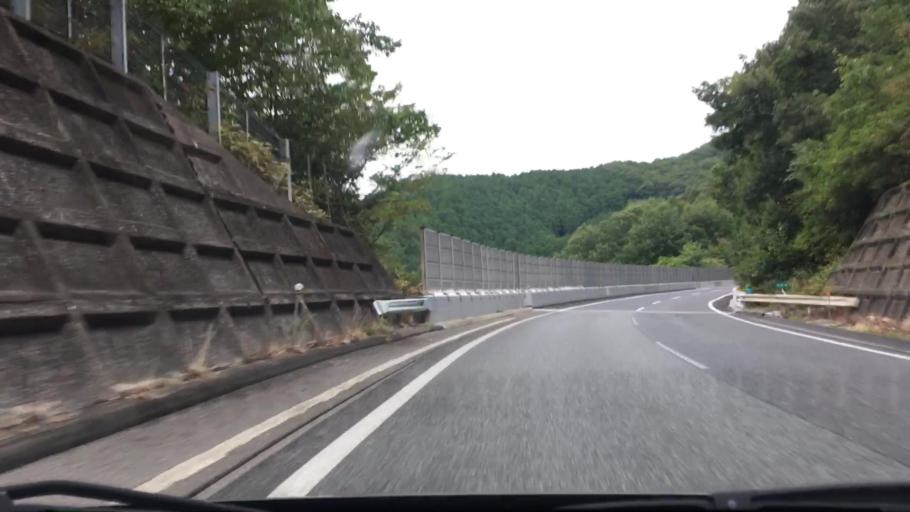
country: JP
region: Okayama
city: Niimi
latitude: 34.9903
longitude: 133.4605
